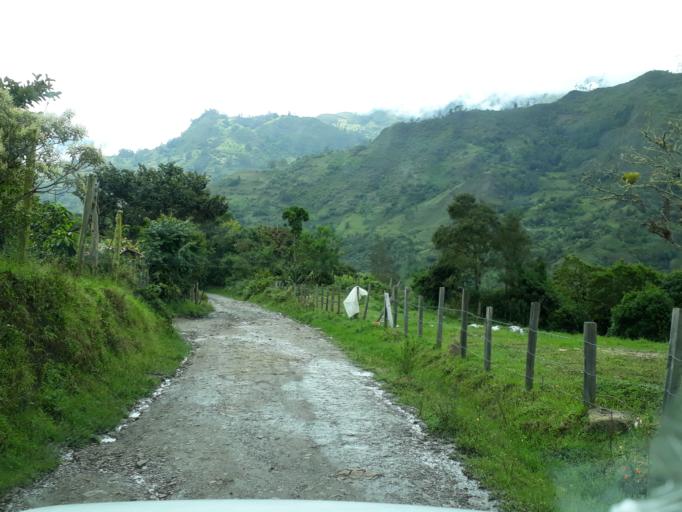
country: CO
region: Cundinamarca
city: Gacheta
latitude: 4.8566
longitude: -73.6450
